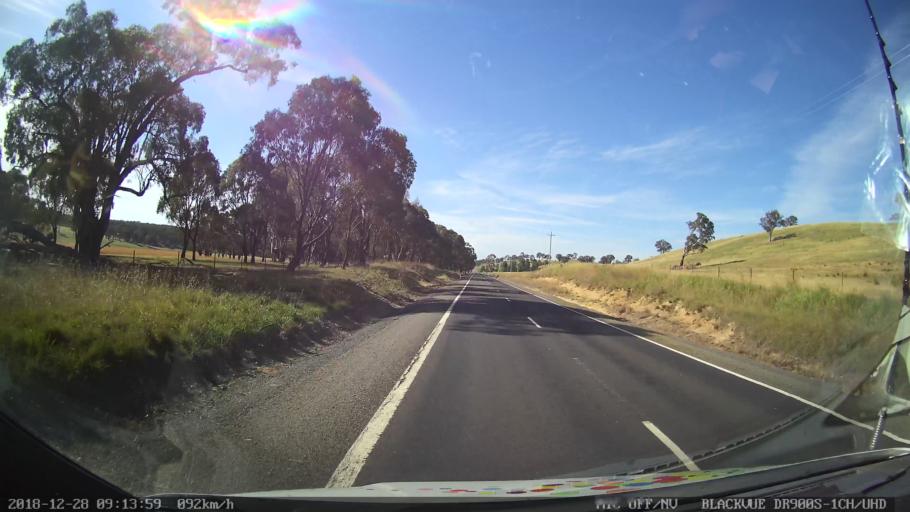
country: AU
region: New South Wales
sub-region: Upper Lachlan Shire
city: Crookwell
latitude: -34.2762
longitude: 149.3450
